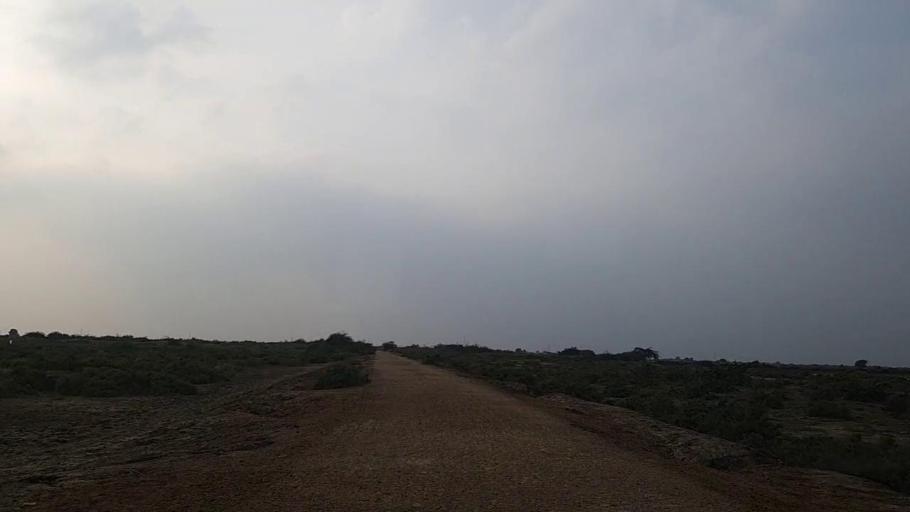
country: PK
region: Sindh
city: Mirpur Sakro
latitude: 24.6140
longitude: 67.5146
